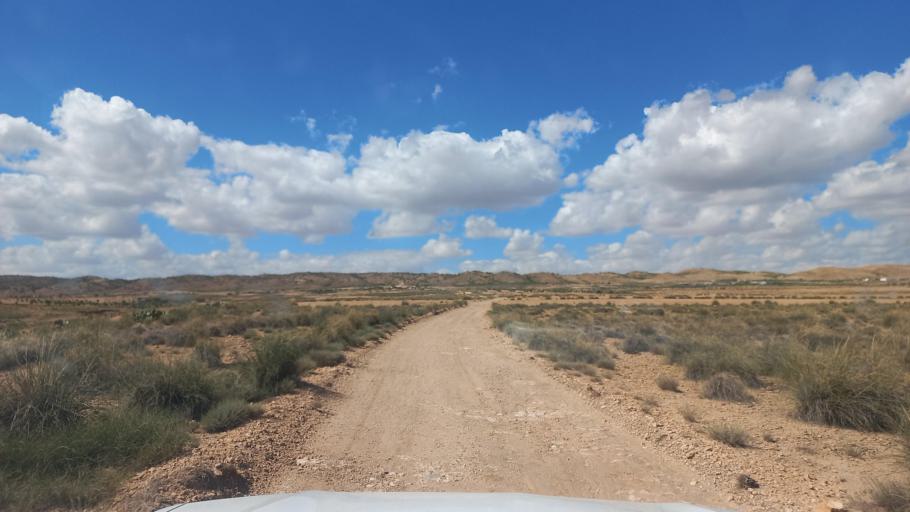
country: TN
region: Al Qasrayn
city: Sbiba
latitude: 35.3567
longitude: 9.0097
